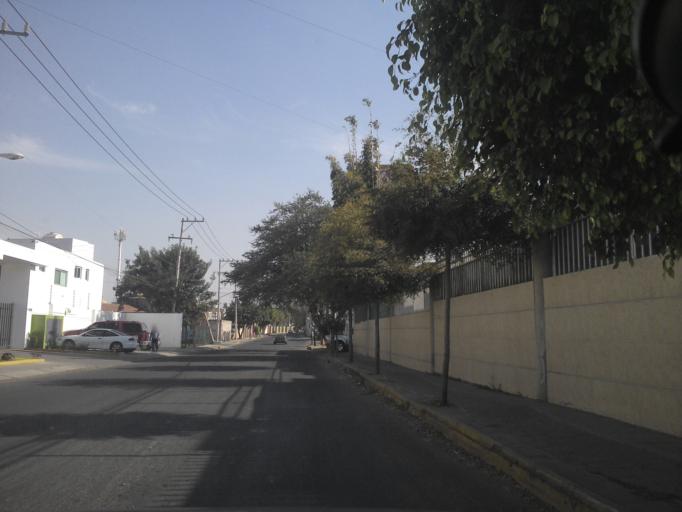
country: MX
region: Jalisco
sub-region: Tlajomulco de Zuniga
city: Palomar
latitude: 20.6135
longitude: -103.4544
